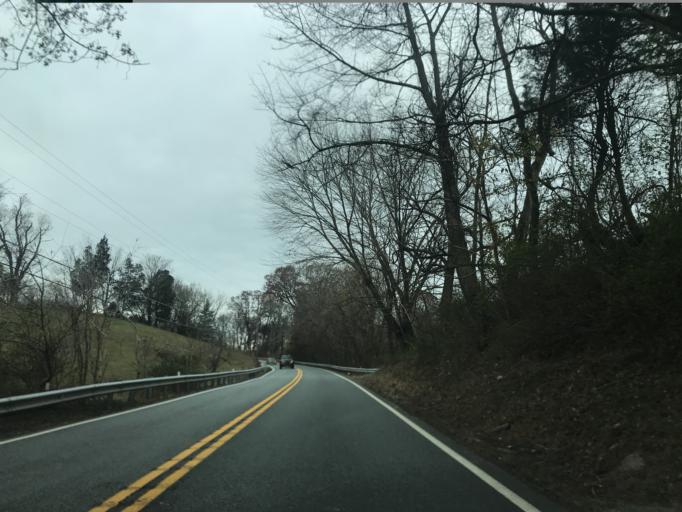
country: US
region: Maryland
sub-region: Harford County
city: Bel Air North
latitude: 39.6161
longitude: -76.3321
